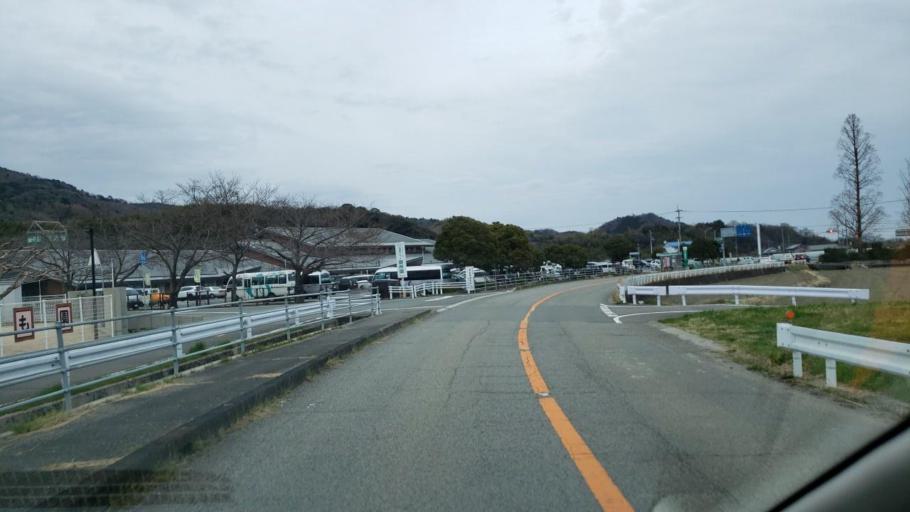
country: JP
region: Tokushima
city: Kamojimacho-jogejima
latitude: 34.1232
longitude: 134.3521
